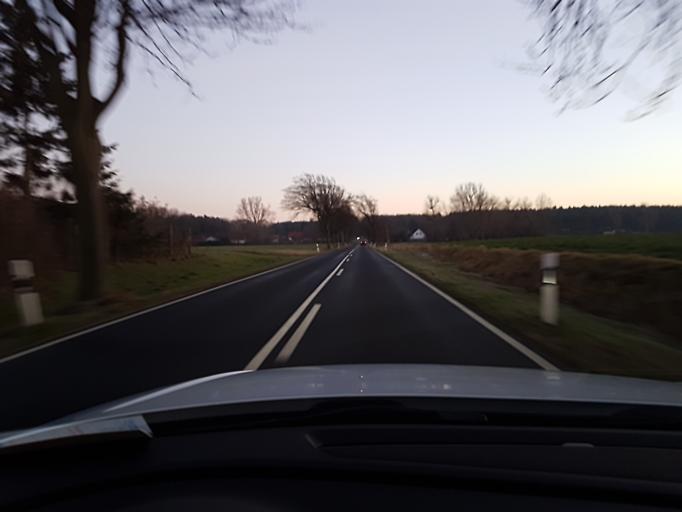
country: DE
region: Mecklenburg-Vorpommern
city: Gingst
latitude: 54.5120
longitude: 13.2712
